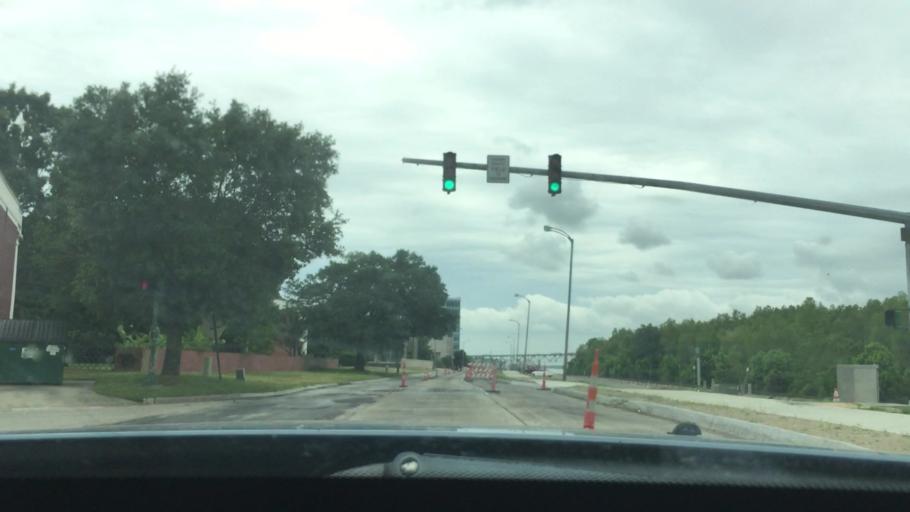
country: US
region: Louisiana
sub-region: West Baton Rouge Parish
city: Port Allen
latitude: 30.4562
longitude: -91.1900
